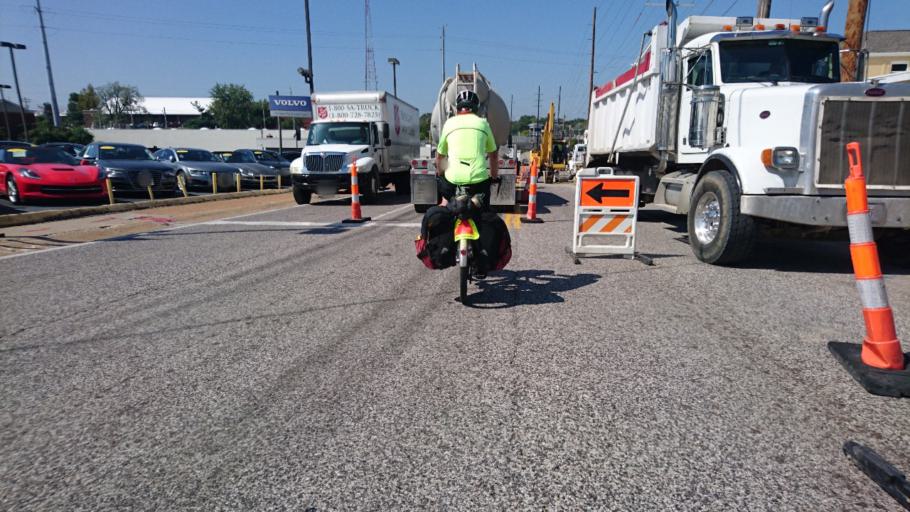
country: US
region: Missouri
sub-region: Saint Louis County
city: Maplewood
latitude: 38.6132
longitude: -90.3285
